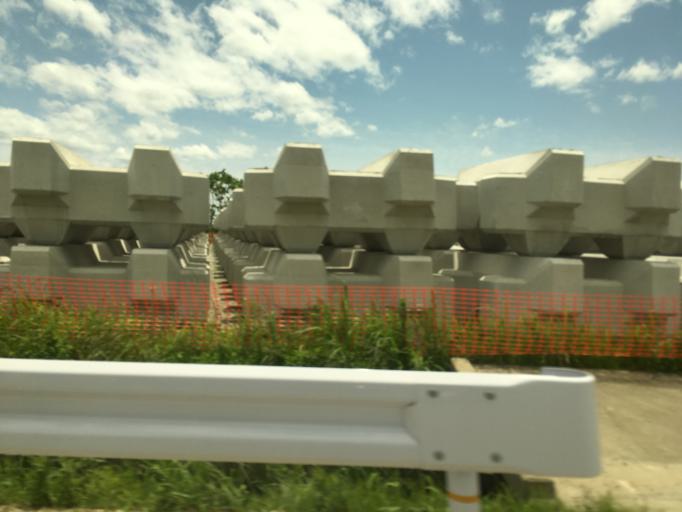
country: JP
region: Fukushima
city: Namie
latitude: 37.4924
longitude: 141.0310
